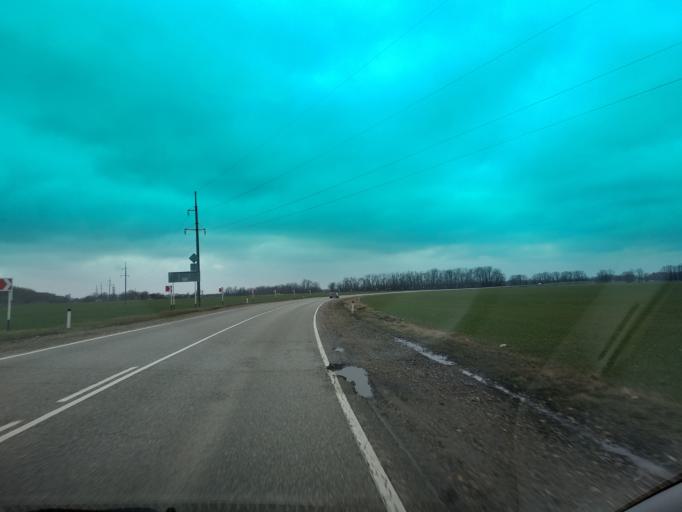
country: RU
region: Krasnodarskiy
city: Novorozhdestvenskaya
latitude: 45.7693
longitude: 39.9570
